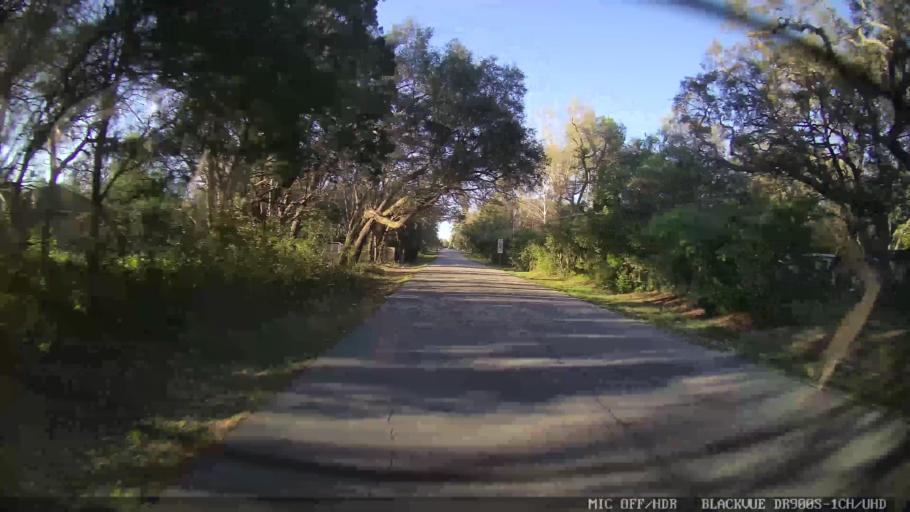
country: US
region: Florida
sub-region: Pasco County
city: Shady Hills
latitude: 28.4067
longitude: -82.5737
